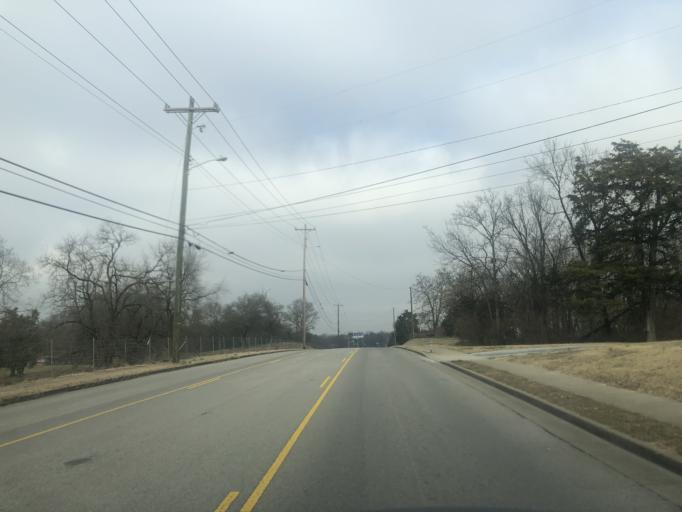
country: US
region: Tennessee
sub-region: Rutherford County
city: La Vergne
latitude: 36.0698
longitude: -86.6396
